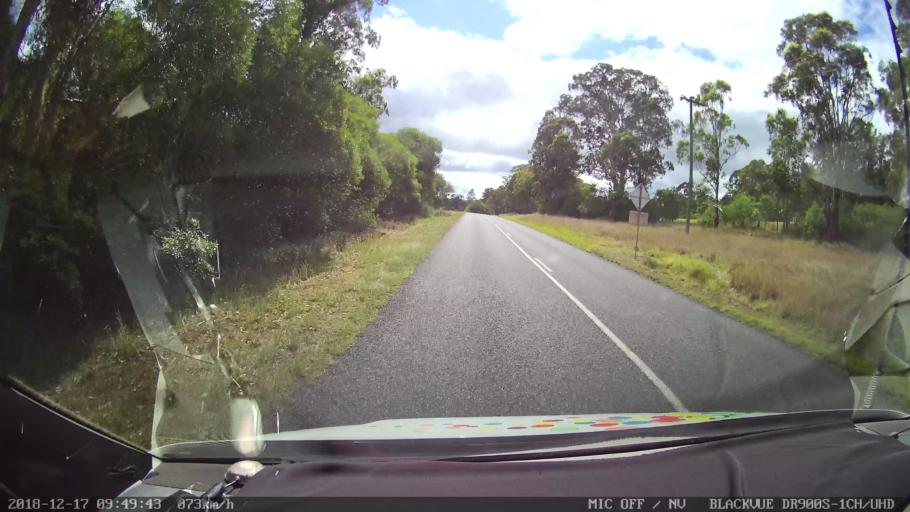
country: AU
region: New South Wales
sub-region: Tenterfield Municipality
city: Carrolls Creek
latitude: -28.9253
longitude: 152.3556
